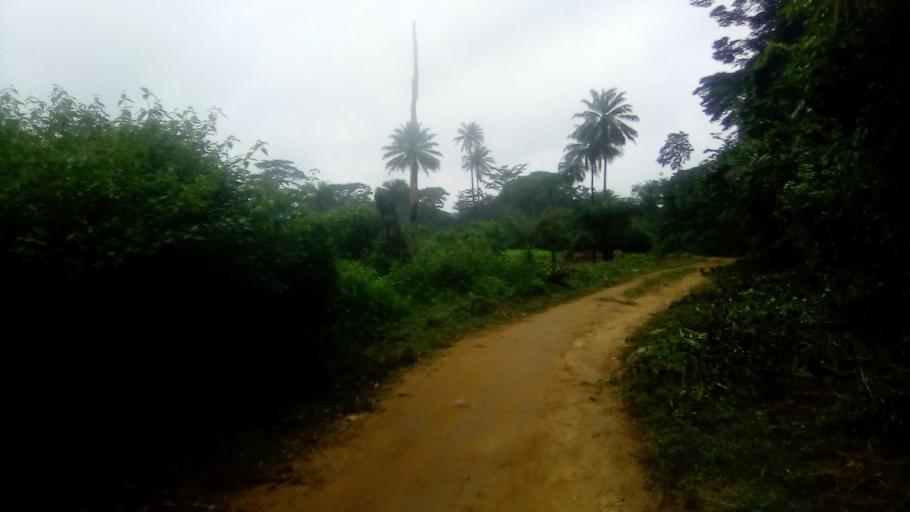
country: SL
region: Eastern Province
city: Kailahun
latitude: 8.2918
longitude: -10.5980
